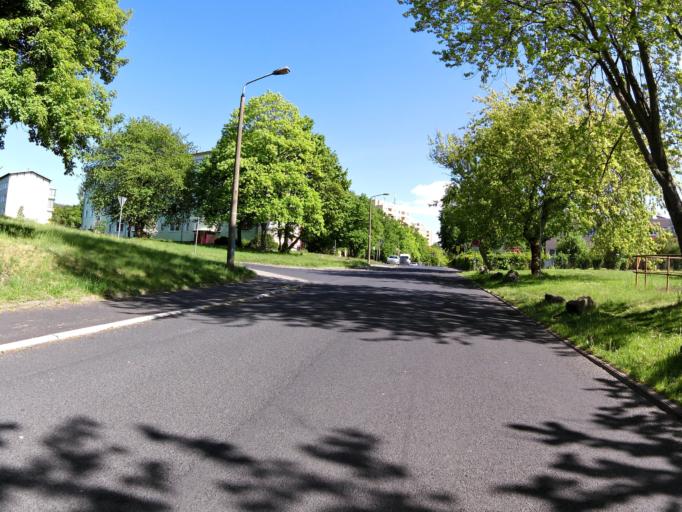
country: DE
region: Thuringia
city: Leimbach
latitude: 50.8105
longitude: 10.2149
